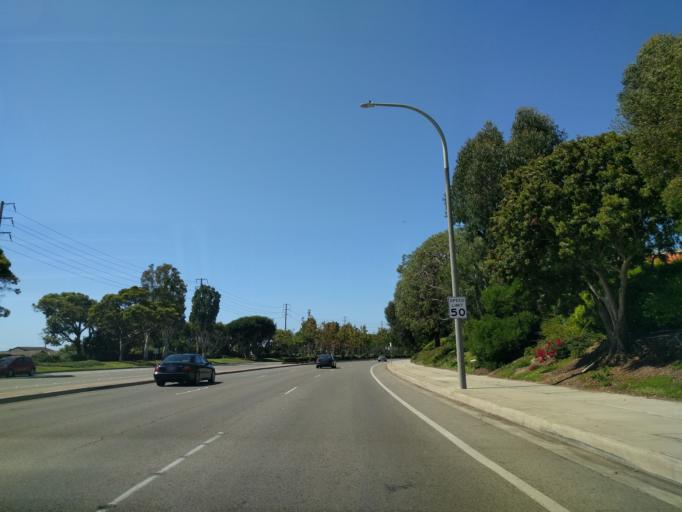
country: US
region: California
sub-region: Orange County
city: San Joaquin Hills
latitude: 33.6076
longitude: -117.8599
